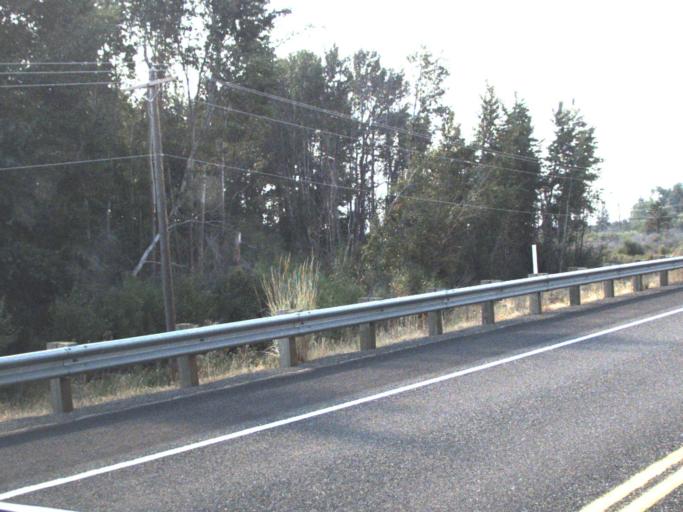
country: US
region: Washington
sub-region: Kittitas County
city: Ellensburg
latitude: 47.1054
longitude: -120.6634
